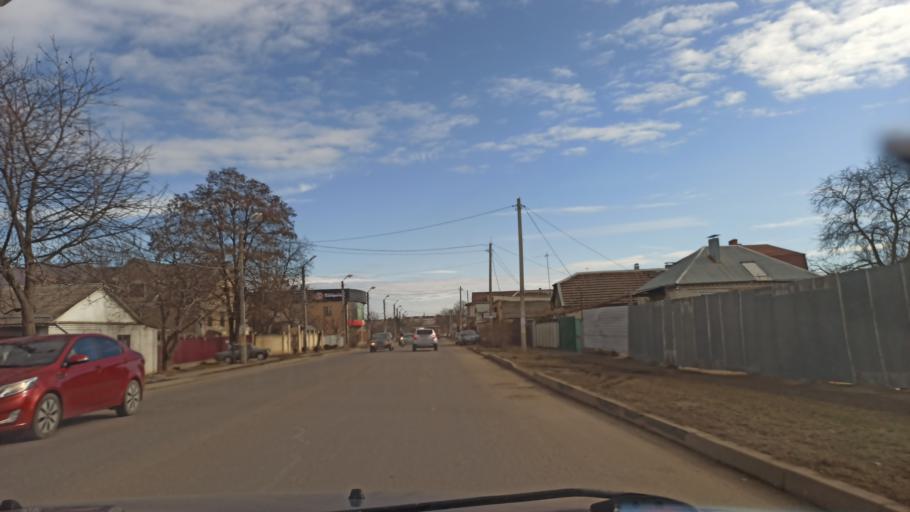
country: RU
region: Stavropol'skiy
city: Svobody
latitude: 44.0332
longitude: 43.0368
